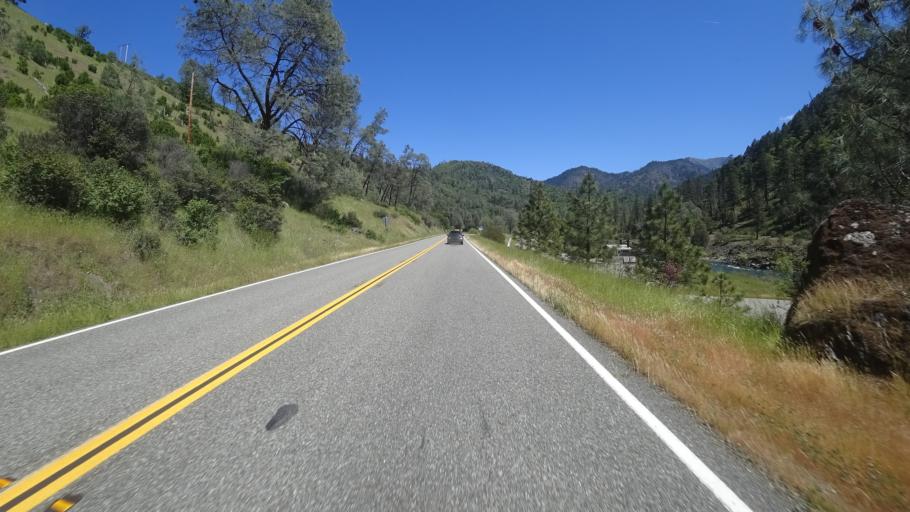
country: US
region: California
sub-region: Trinity County
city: Hayfork
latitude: 40.7412
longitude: -123.2181
